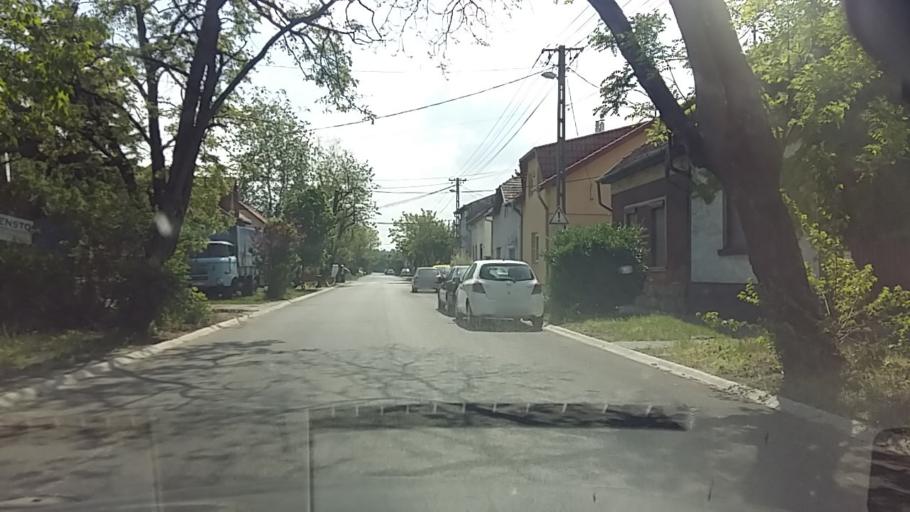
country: HU
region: Budapest
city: Budapest XV. keruelet
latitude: 47.5603
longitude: 19.1263
